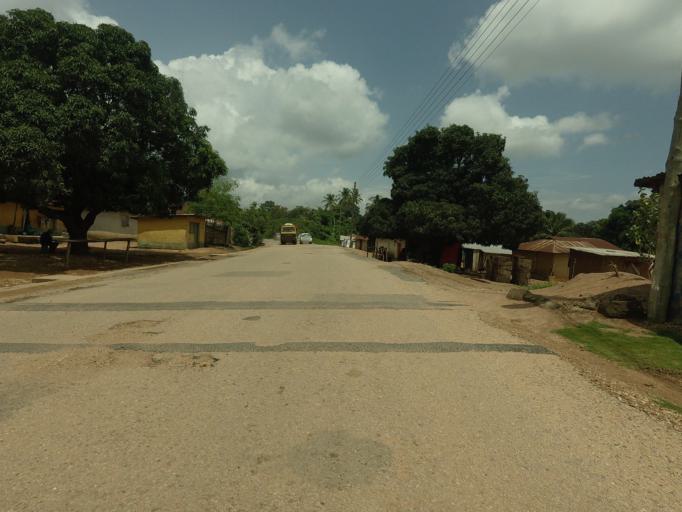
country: GH
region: Volta
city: Ho
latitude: 6.7239
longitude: 0.3419
